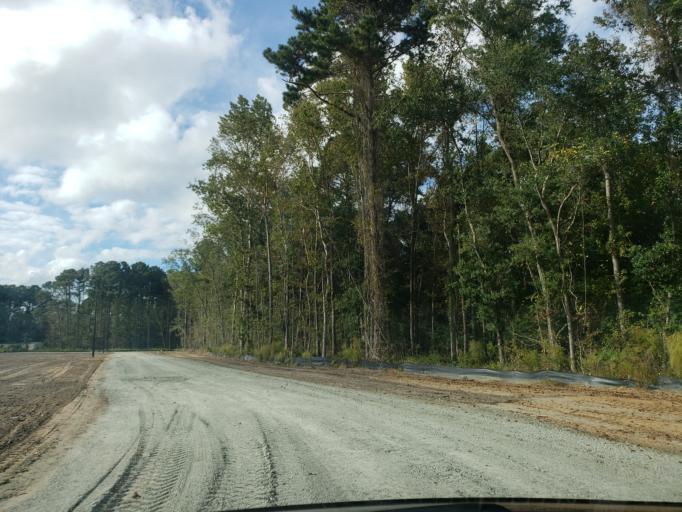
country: US
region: Georgia
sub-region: Bryan County
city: Richmond Hill
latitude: 32.0072
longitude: -81.2937
